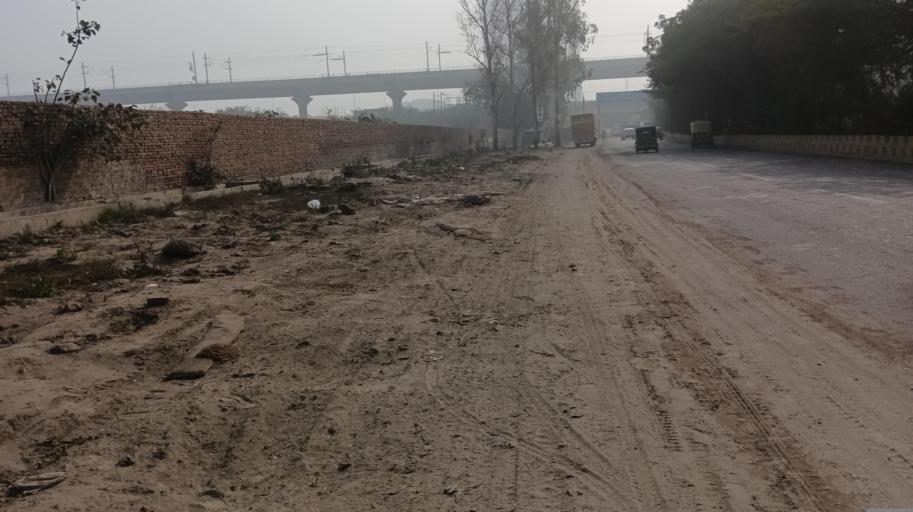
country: IN
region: Uttar Pradesh
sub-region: Ghaziabad
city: Ghaziabad
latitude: 28.6698
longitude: 77.3689
